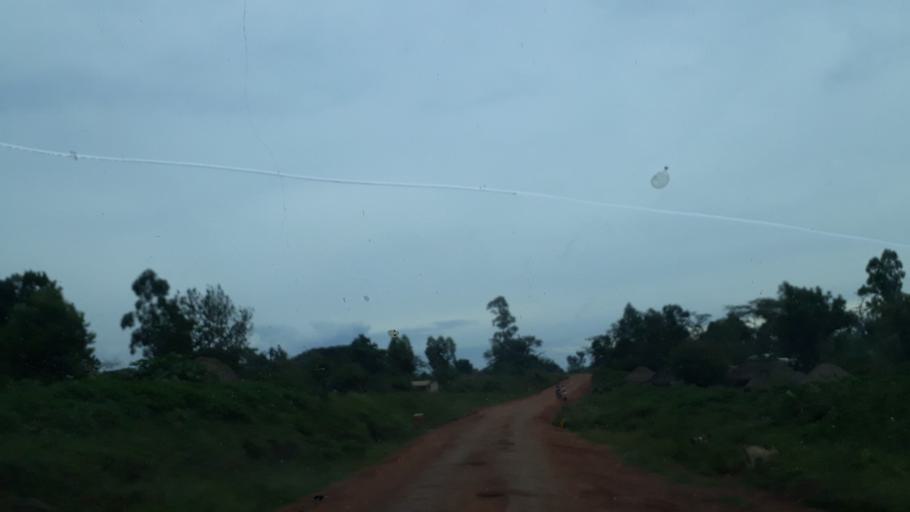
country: UG
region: Northern Region
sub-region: Zombo District
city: Paidha
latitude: 2.1853
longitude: 30.7256
